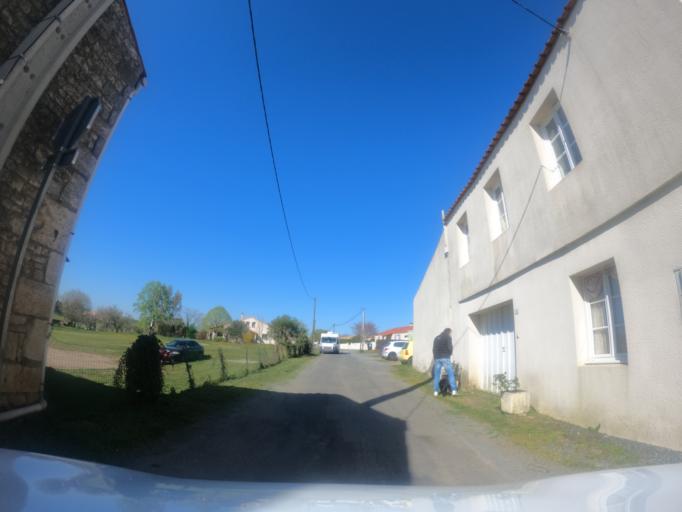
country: FR
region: Pays de la Loire
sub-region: Departement de la Vendee
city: Fontenay-le-Comte
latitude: 46.4241
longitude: -0.8162
